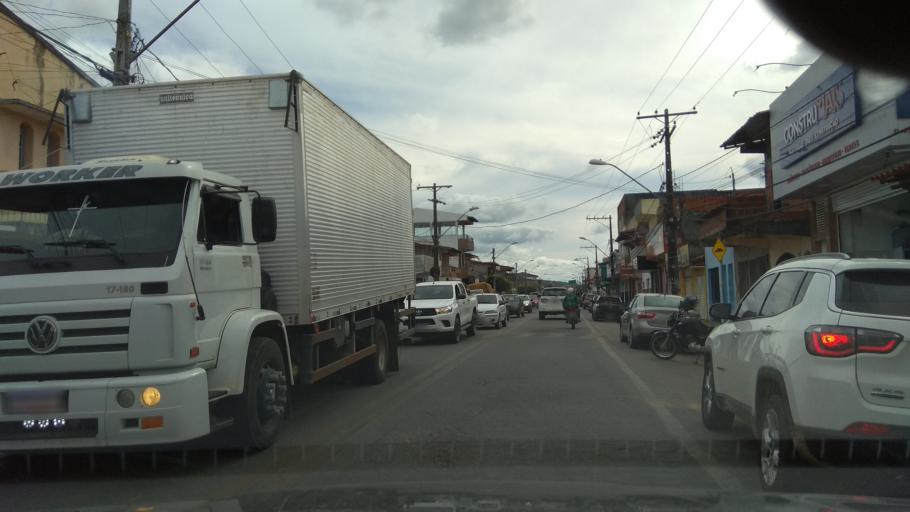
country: BR
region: Bahia
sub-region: Ipiau
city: Ipiau
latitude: -14.1359
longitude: -39.7412
